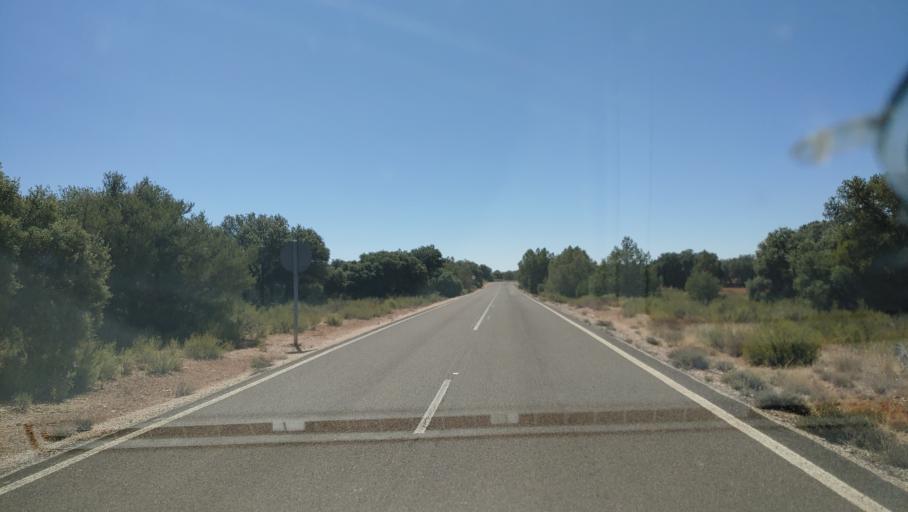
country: ES
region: Castille-La Mancha
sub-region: Provincia de Albacete
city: Ossa de Montiel
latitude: 38.8820
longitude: -2.7768
